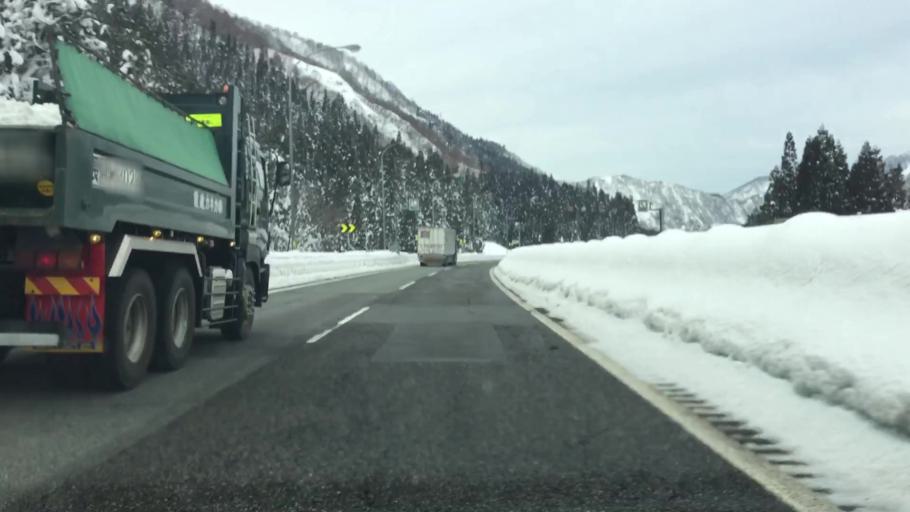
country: JP
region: Niigata
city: Shiozawa
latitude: 36.8864
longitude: 138.8500
